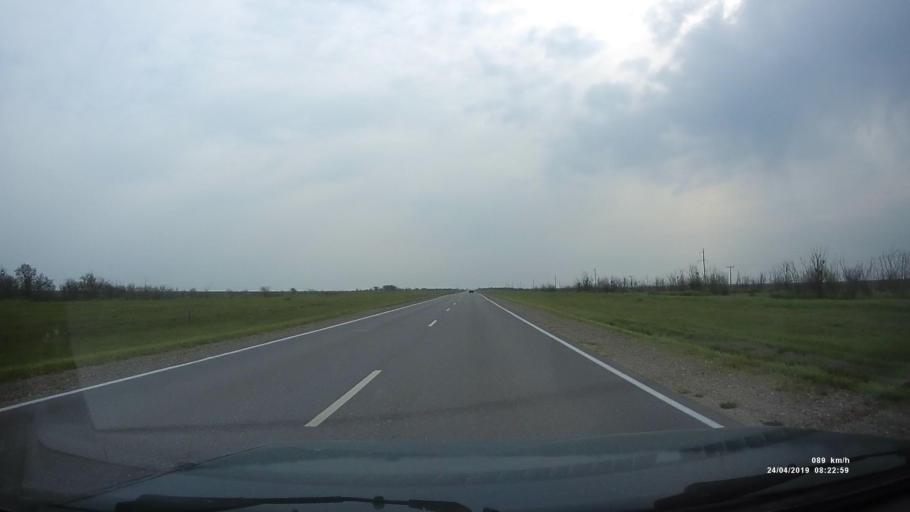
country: RU
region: Kalmykiya
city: Priyutnoye
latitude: 46.1157
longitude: 43.7284
